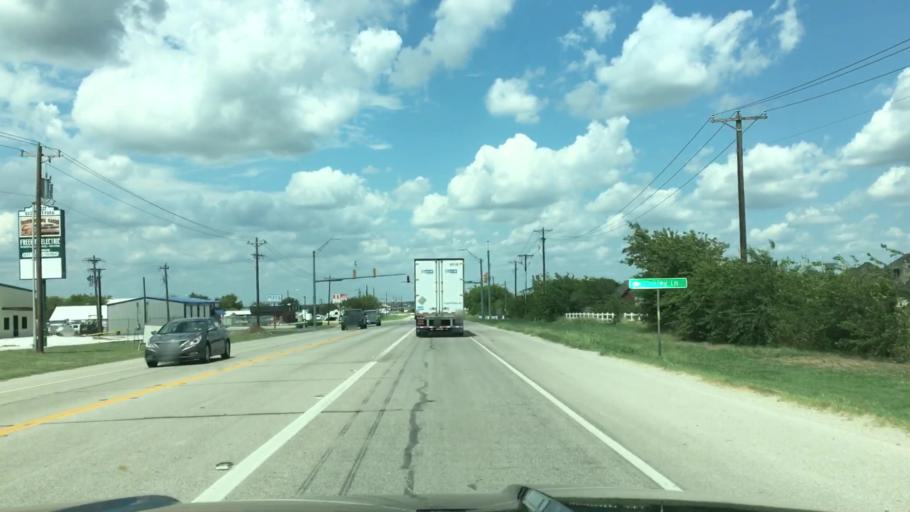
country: US
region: Texas
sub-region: Tarrant County
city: Pecan Acres
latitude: 32.9518
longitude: -97.4207
